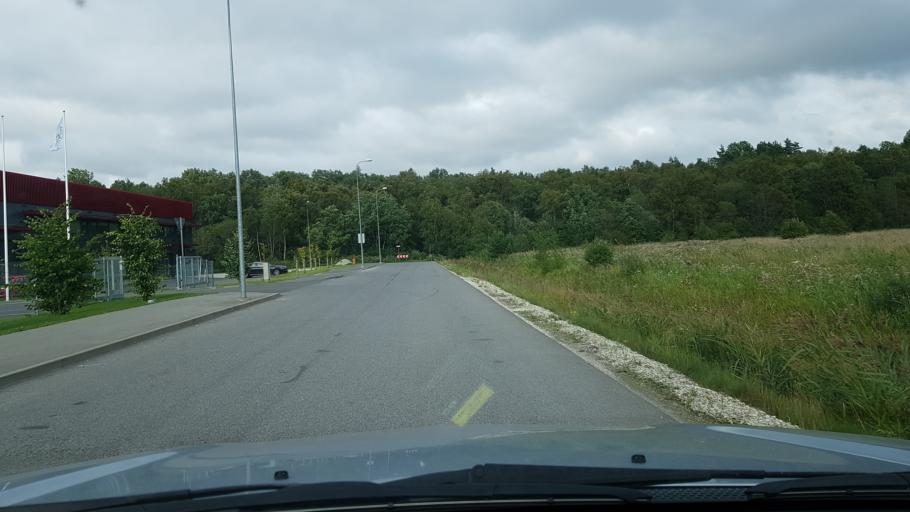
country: EE
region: Harju
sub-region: Tallinna linn
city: Kose
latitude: 59.3987
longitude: 24.8281
